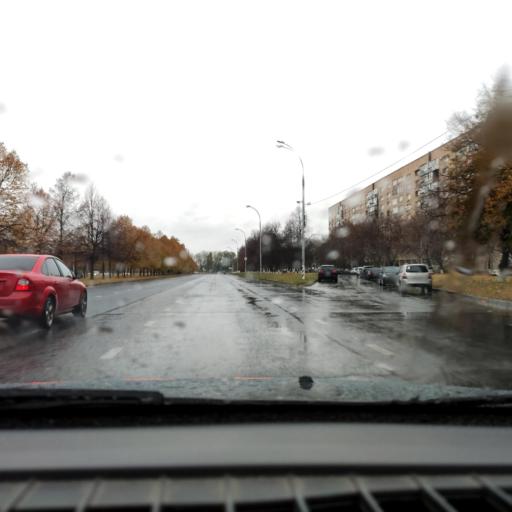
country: RU
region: Samara
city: Tol'yatti
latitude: 53.5213
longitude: 49.2651
